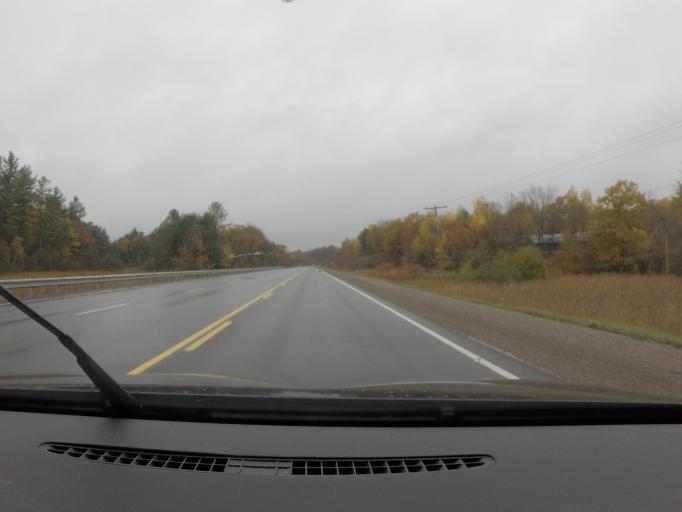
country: CA
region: Ontario
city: Greater Napanee
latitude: 44.6643
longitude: -77.0807
